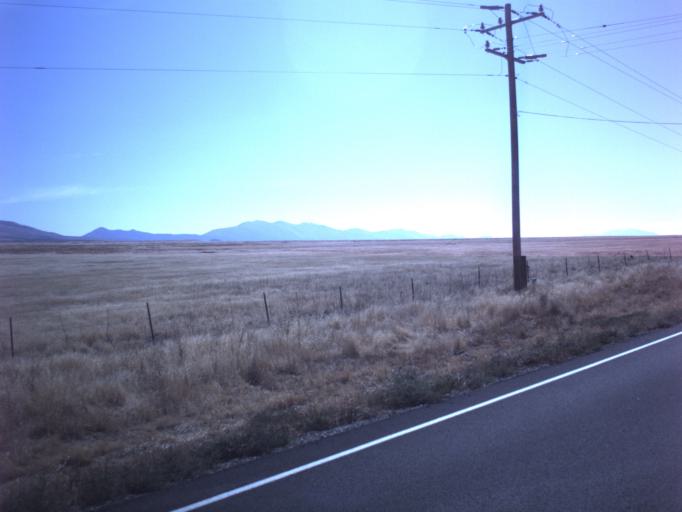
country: US
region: Utah
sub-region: Tooele County
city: Grantsville
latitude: 40.4339
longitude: -112.7487
